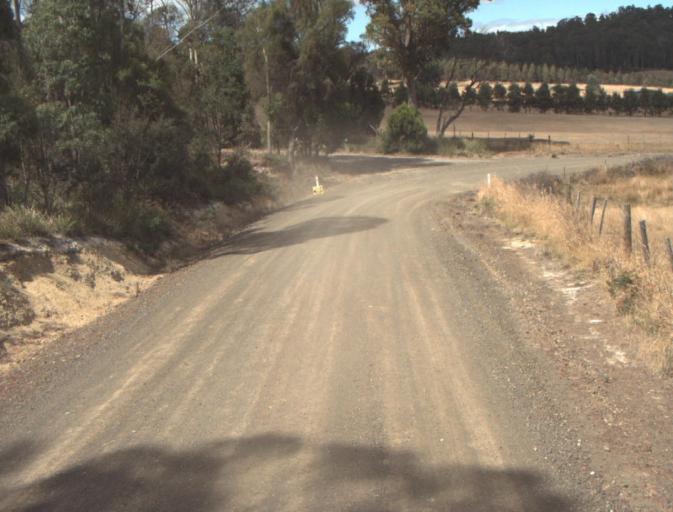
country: AU
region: Tasmania
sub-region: Launceston
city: Mayfield
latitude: -41.2182
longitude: 147.1672
